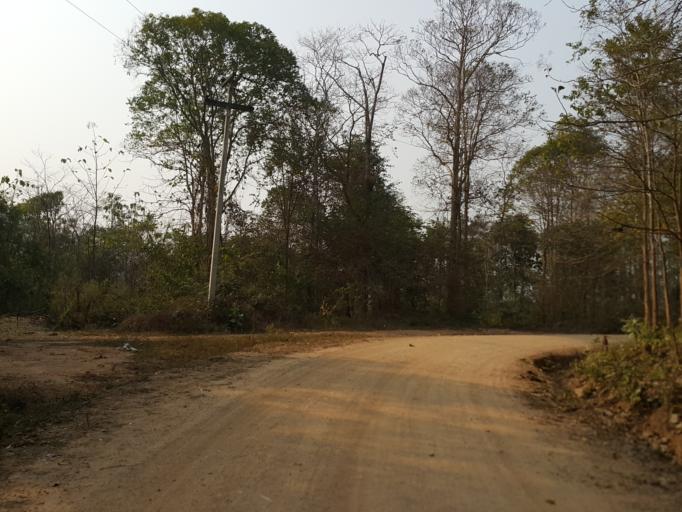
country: TH
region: Lamphun
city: Li
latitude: 17.6004
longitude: 98.9712
